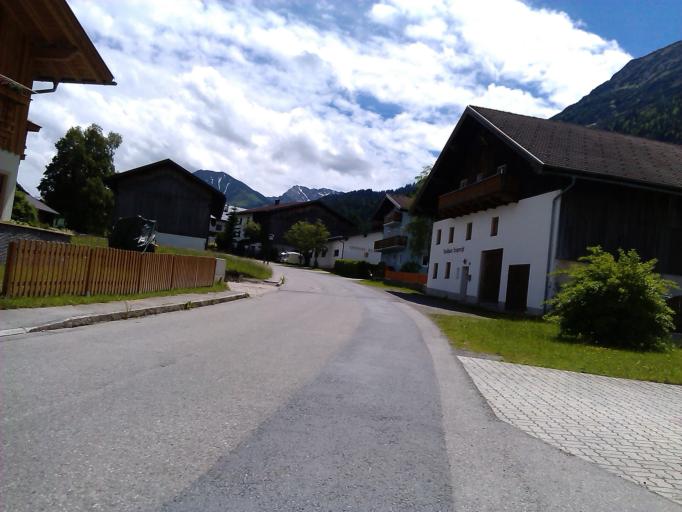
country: AT
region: Tyrol
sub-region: Politischer Bezirk Reutte
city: Heiterwang
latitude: 47.4448
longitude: 10.7437
